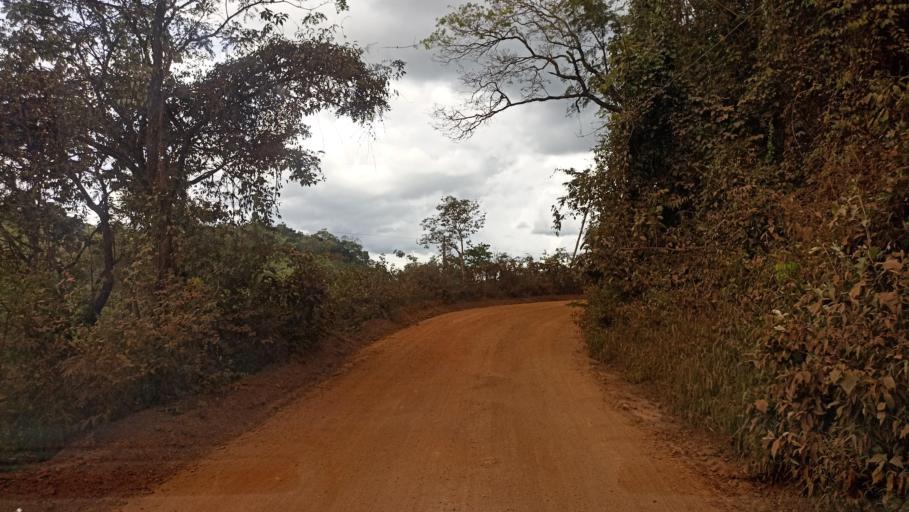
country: BR
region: Minas Gerais
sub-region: Itabirito
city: Itabirito
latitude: -20.3587
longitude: -43.7674
